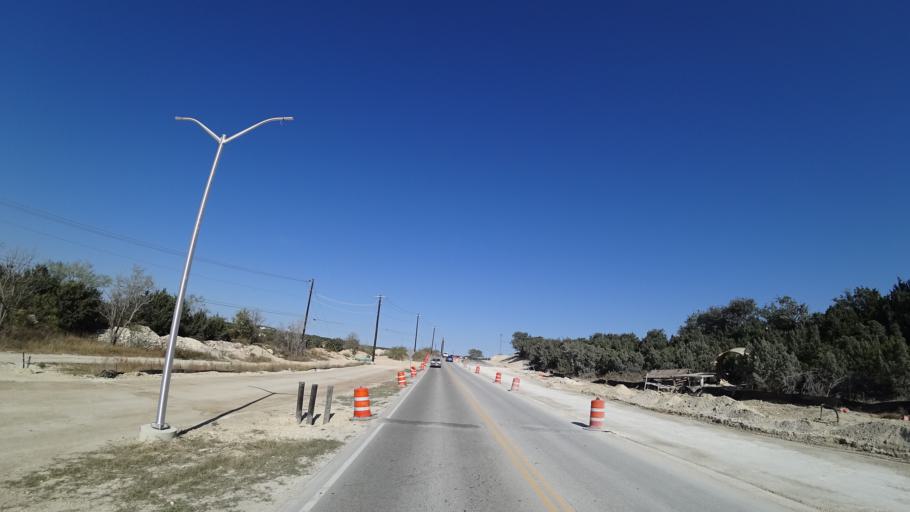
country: US
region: Texas
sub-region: Williamson County
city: Cedar Park
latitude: 30.5053
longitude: -97.8566
